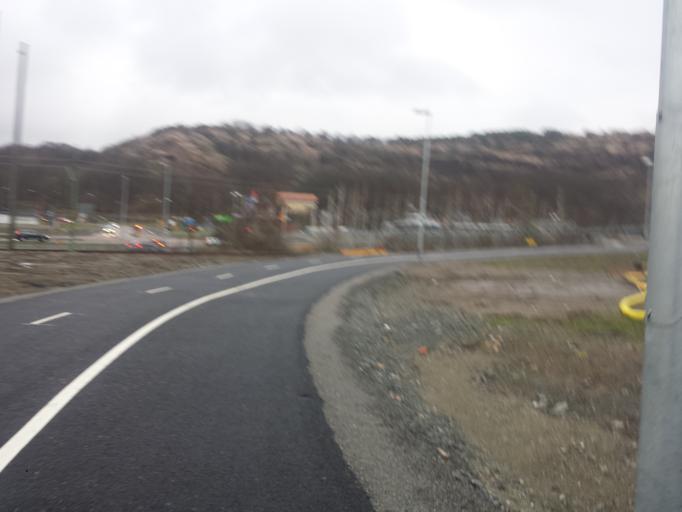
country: SE
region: Vaestra Goetaland
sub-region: Goteborg
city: Majorna
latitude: 57.7108
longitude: 11.9310
